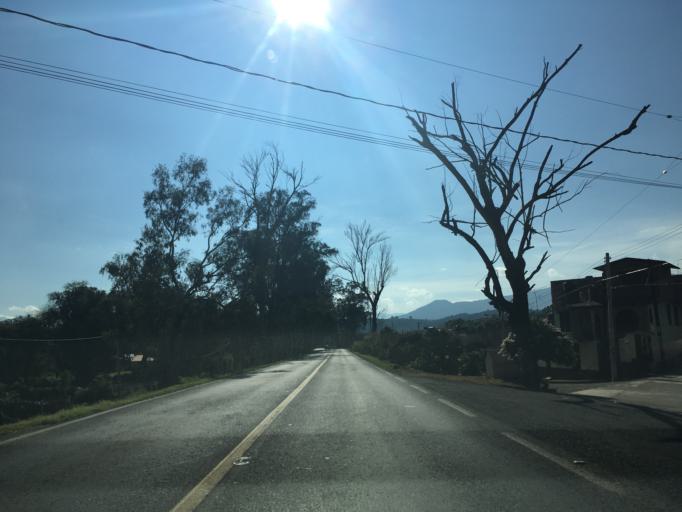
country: MX
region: Mexico
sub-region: Chalco
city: Chilchota
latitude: 19.8514
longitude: -102.1276
